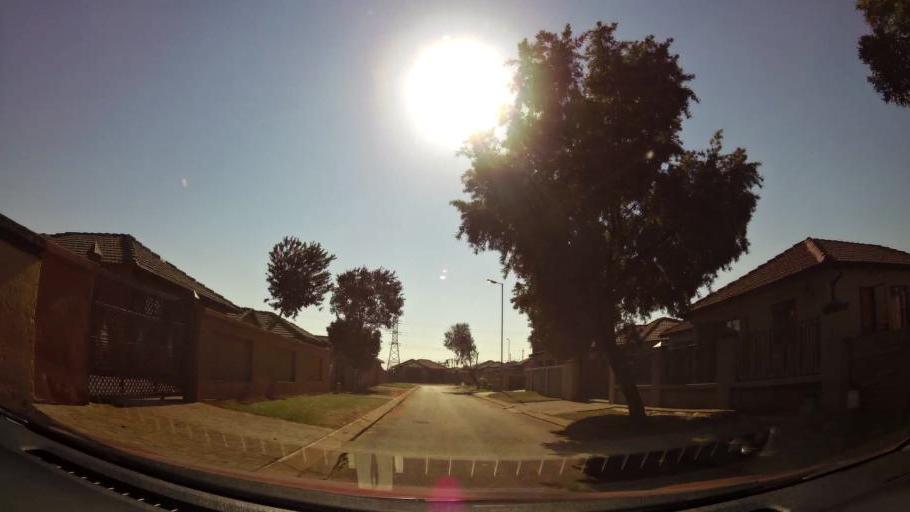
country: ZA
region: North-West
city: Ga-Rankuwa
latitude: -25.6372
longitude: 28.0882
